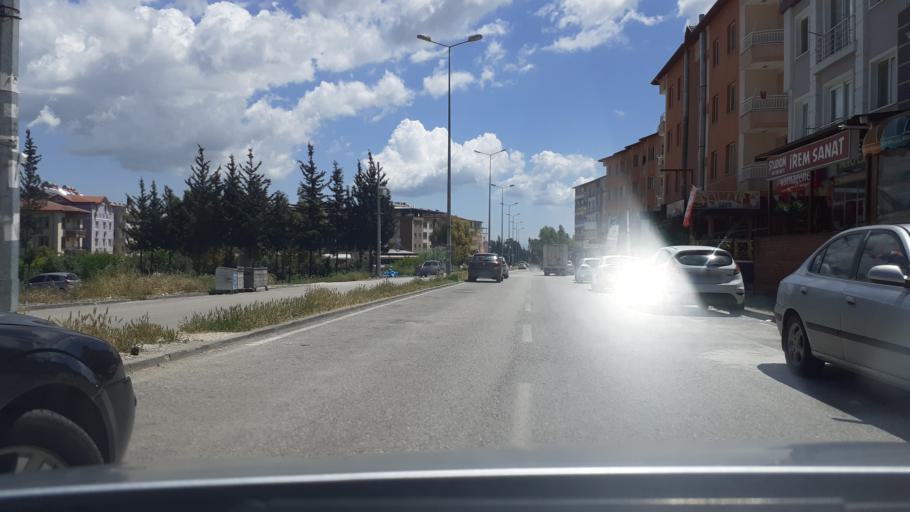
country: TR
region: Hatay
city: Anayazi
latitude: 36.3348
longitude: 36.2017
